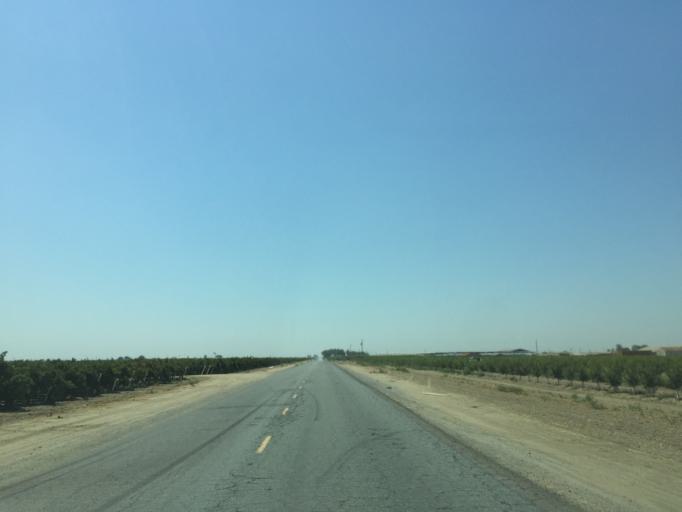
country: US
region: California
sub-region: Tulare County
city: Goshen
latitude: 36.3710
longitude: -119.3549
